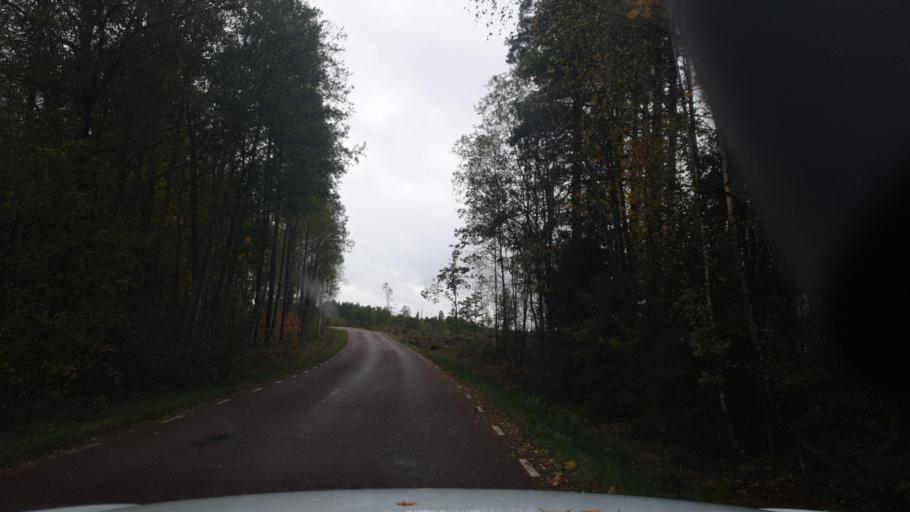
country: SE
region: Vaermland
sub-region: Grums Kommun
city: Grums
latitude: 59.4304
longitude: 13.0846
